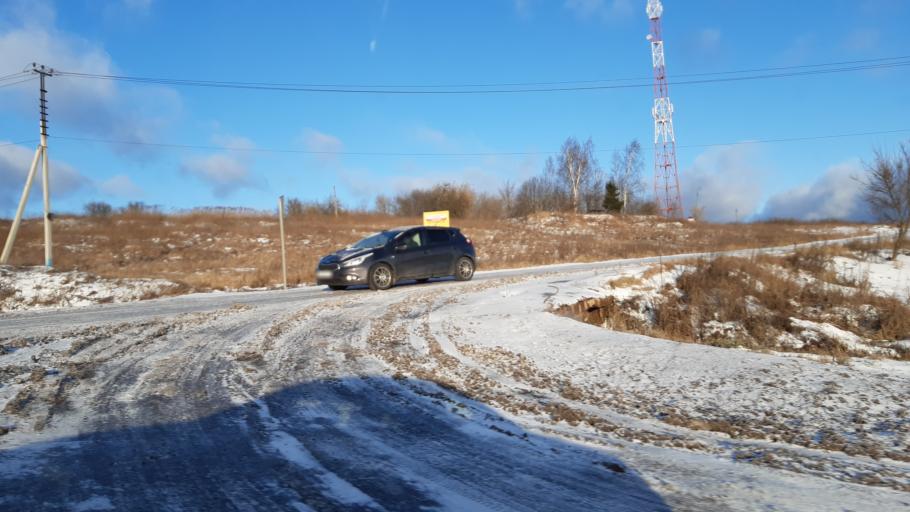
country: RU
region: Vladimir
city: Arsaki
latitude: 56.2843
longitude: 38.3951
